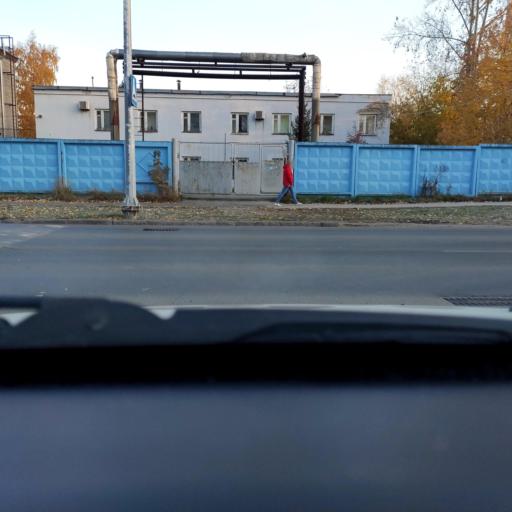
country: RU
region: Perm
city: Kondratovo
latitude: 57.9997
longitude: 56.1705
